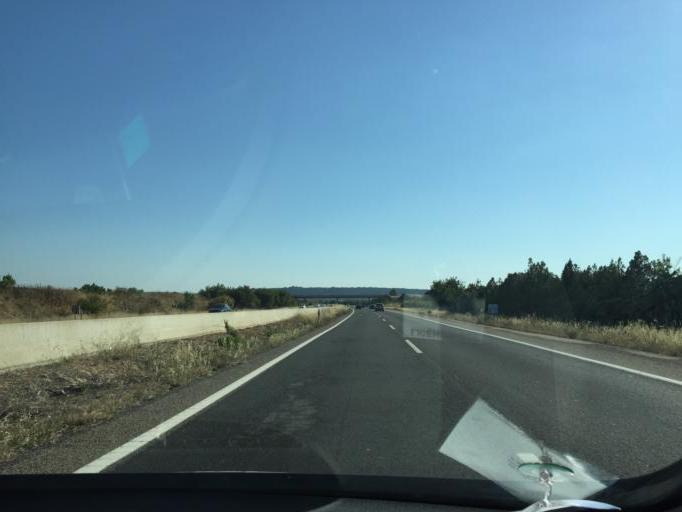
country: ES
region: Balearic Islands
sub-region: Illes Balears
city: Consell
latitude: 39.6590
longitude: 2.8065
